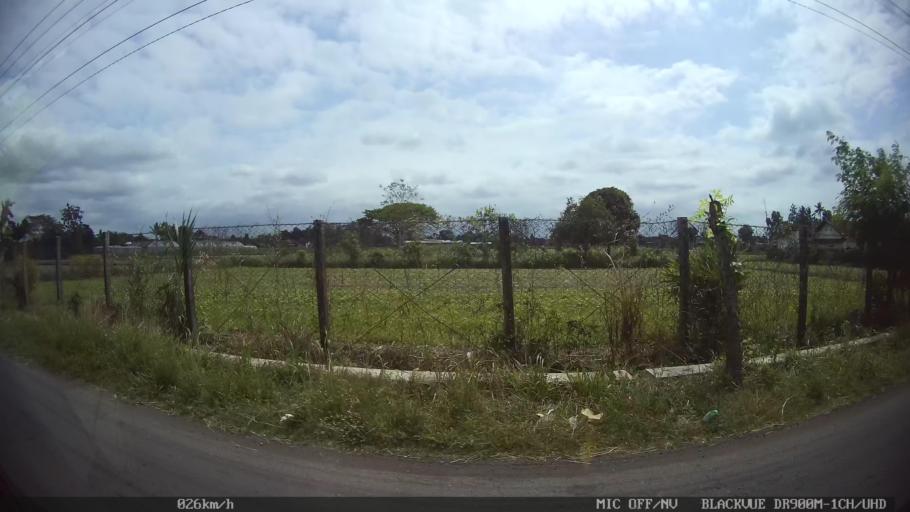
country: ID
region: Daerah Istimewa Yogyakarta
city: Depok
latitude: -7.7910
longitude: 110.4625
